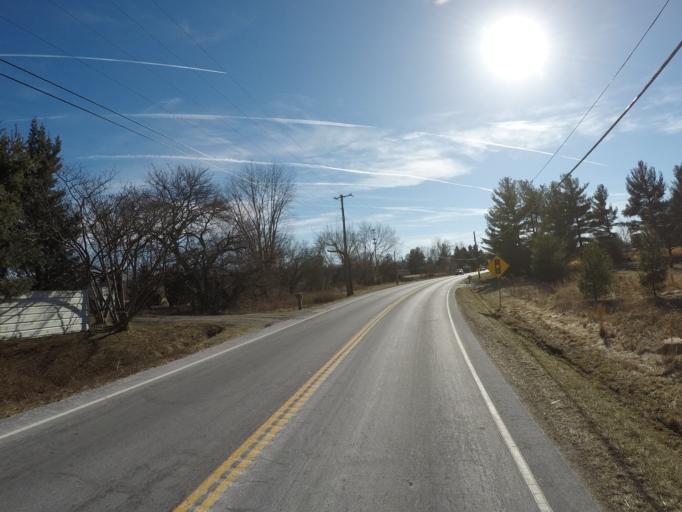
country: US
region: Maryland
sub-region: Frederick County
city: Point of Rocks
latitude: 39.2197
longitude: -77.5337
